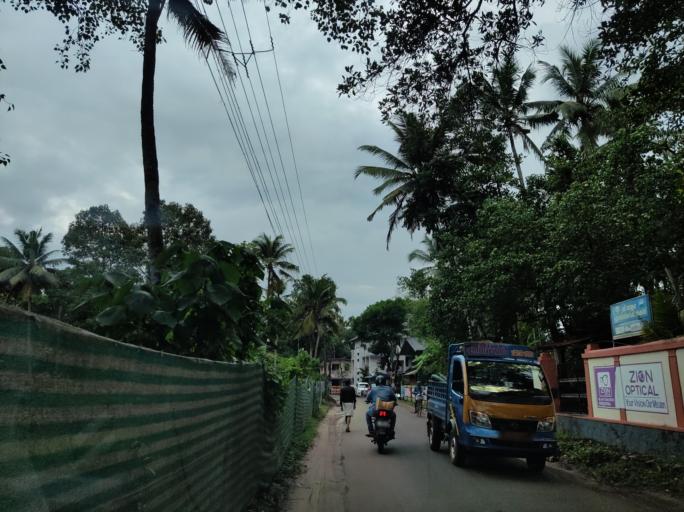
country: IN
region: Kerala
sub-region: Alappuzha
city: Mavelikara
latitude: 9.2418
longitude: 76.5227
